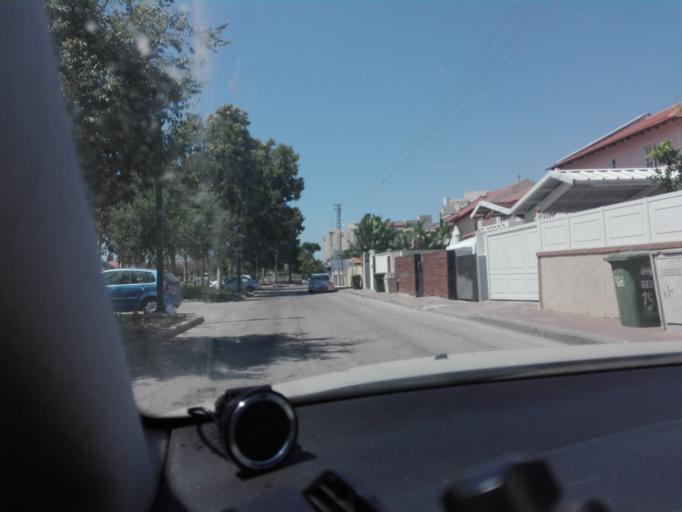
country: IL
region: Central District
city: Bene 'Ayish
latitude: 31.7335
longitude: 34.7453
